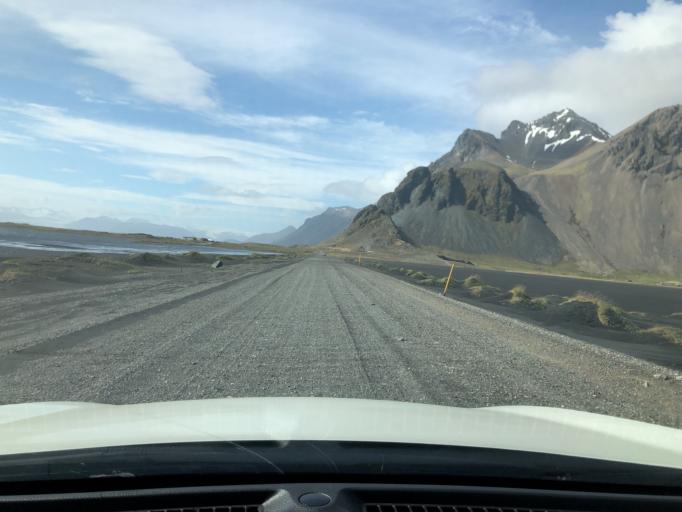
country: IS
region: East
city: Hoefn
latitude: 64.2477
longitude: -14.9791
